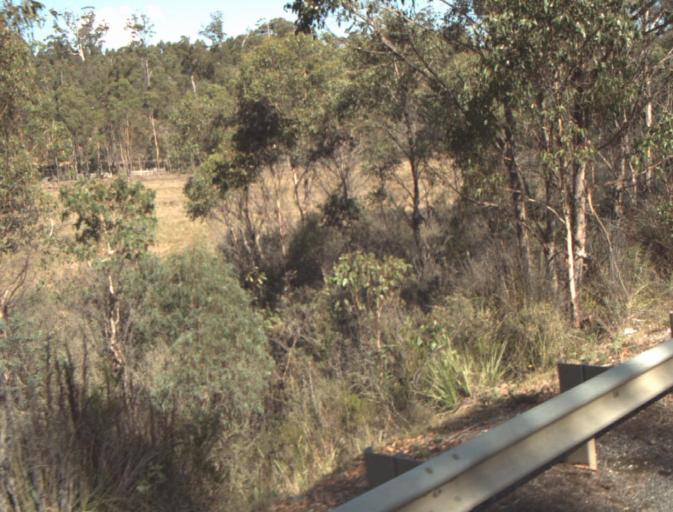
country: AU
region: Tasmania
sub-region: Launceston
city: Mayfield
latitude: -41.3253
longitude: 147.1860
